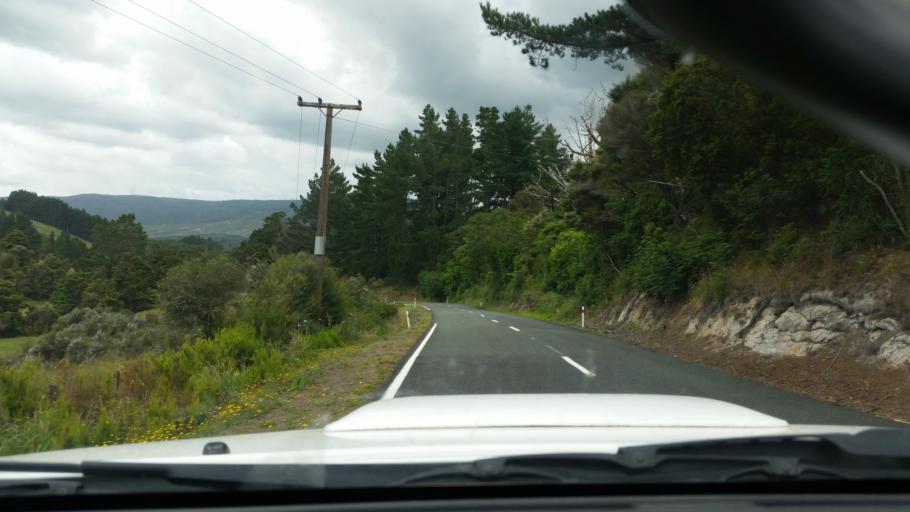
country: NZ
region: Northland
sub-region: Kaipara District
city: Dargaville
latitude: -35.8156
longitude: 173.7263
